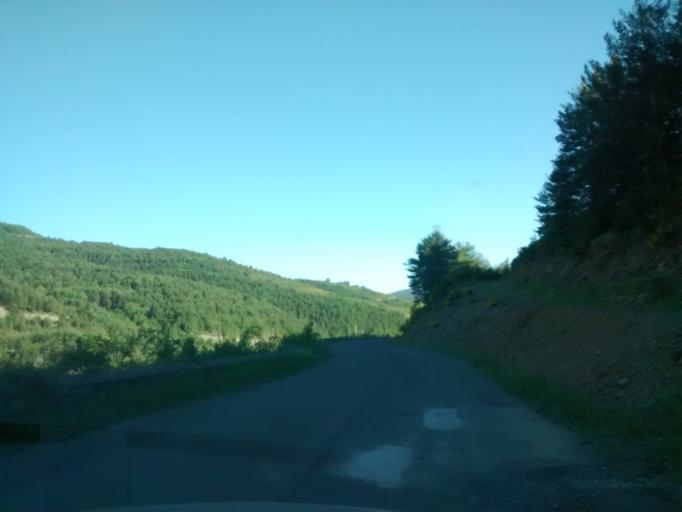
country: ES
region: Aragon
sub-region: Provincia de Huesca
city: Jasa
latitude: 42.6959
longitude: -0.6204
